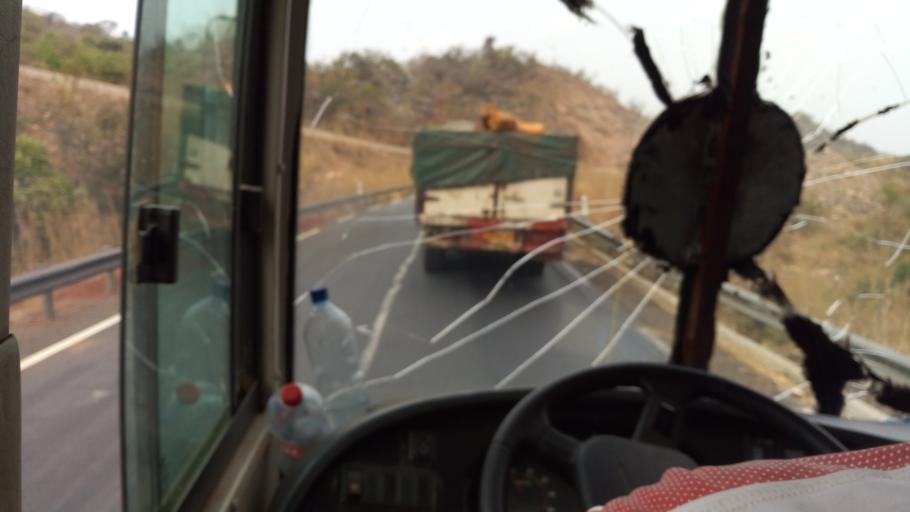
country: TG
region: Kara
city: Bafilo
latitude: 9.2658
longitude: 1.2321
